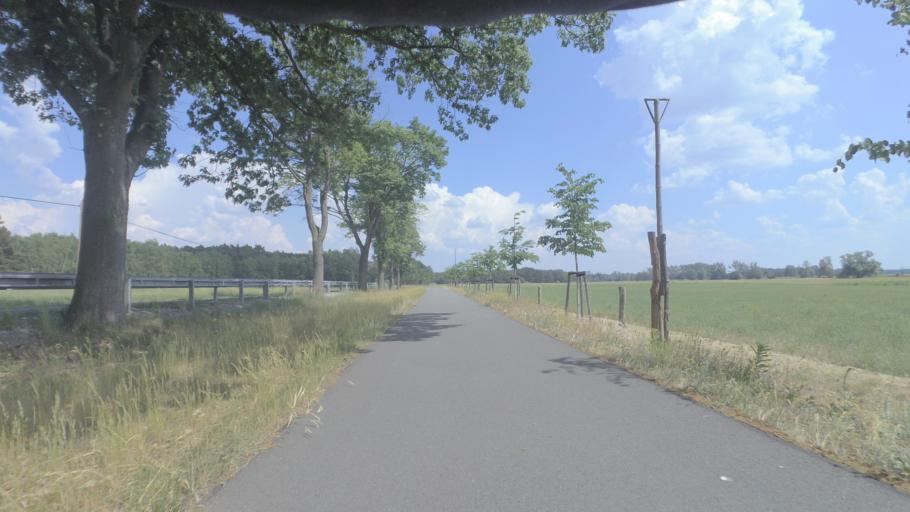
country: DE
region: Brandenburg
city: Beelitz
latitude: 52.2153
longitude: 13.0743
